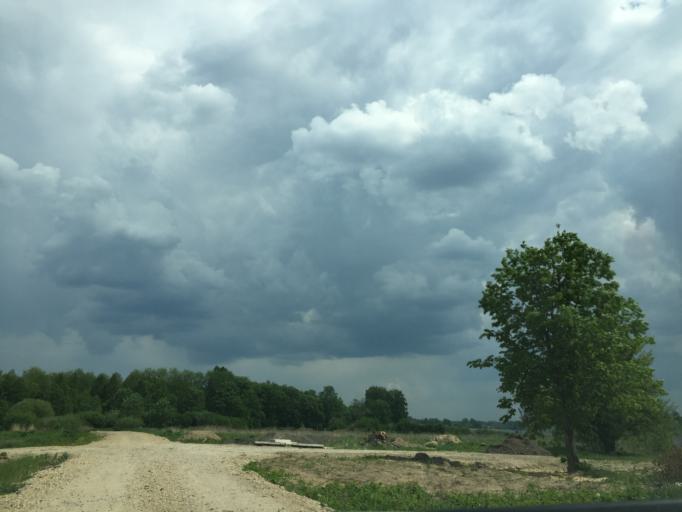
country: LV
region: Plavinu
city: Plavinas
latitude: 56.6172
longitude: 25.7517
